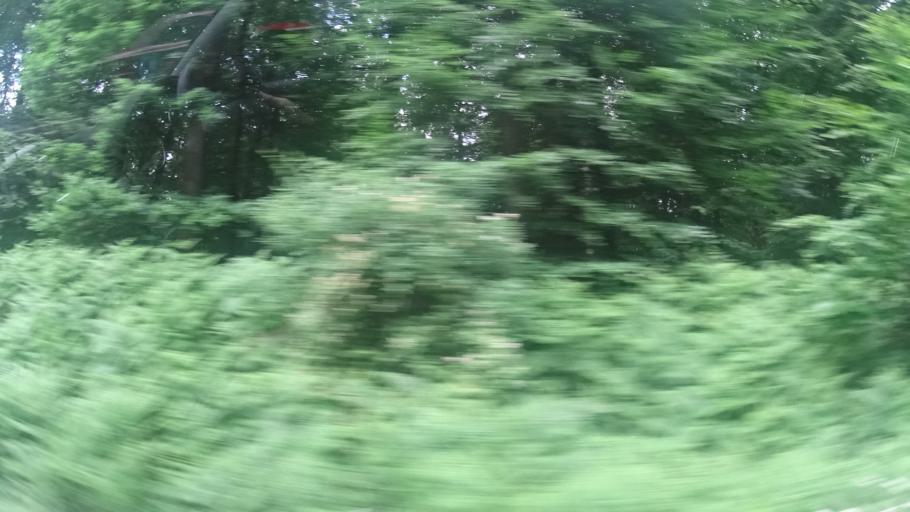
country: DE
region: Lower Saxony
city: Wennigsen
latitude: 52.2322
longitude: 9.6286
